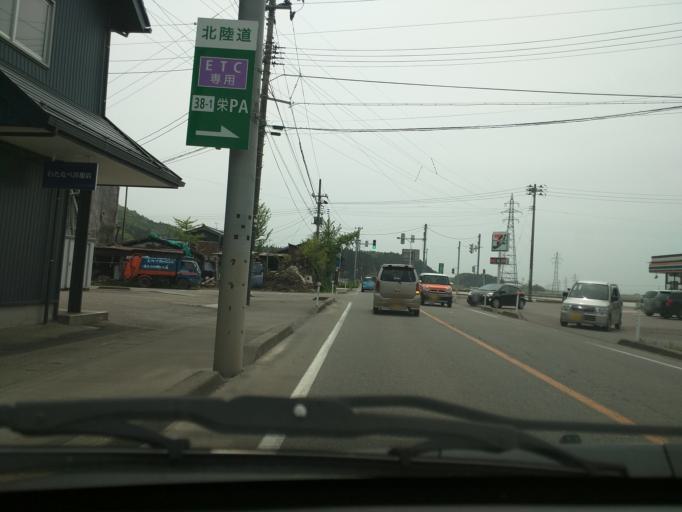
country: JP
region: Niigata
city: Mitsuke
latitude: 37.5711
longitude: 138.9389
